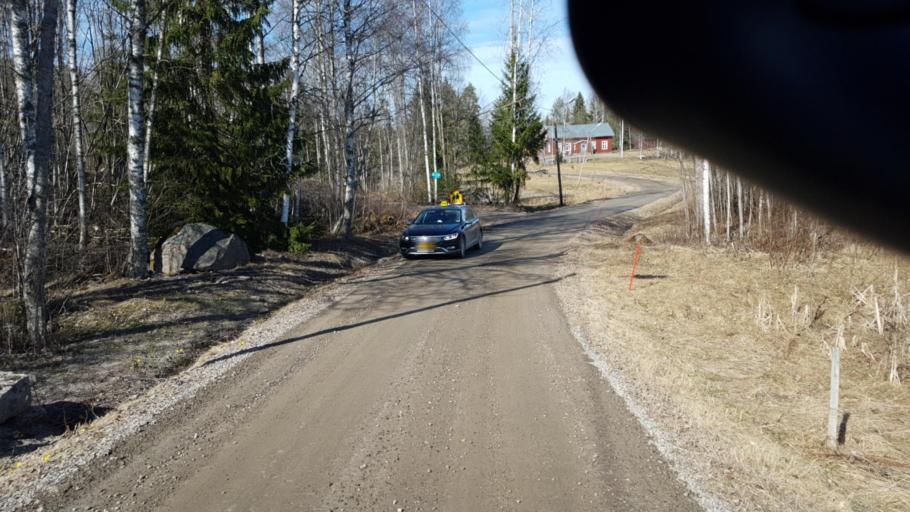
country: SE
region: Vaermland
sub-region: Arvika Kommun
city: Arvika
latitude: 59.6735
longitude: 12.7677
